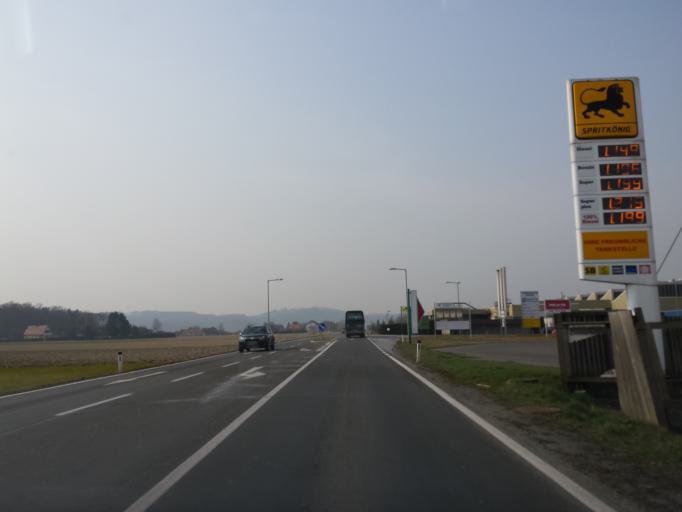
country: AT
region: Styria
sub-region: Politischer Bezirk Hartberg-Fuerstenfeld
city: Fuerstenfeld
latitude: 47.0363
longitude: 16.0931
